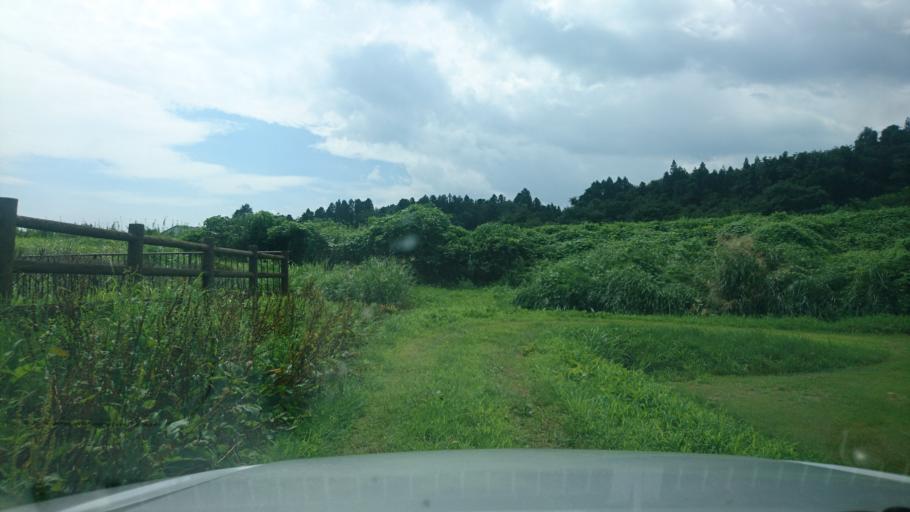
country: JP
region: Iwate
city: Ichinoseki
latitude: 38.7999
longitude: 140.9720
